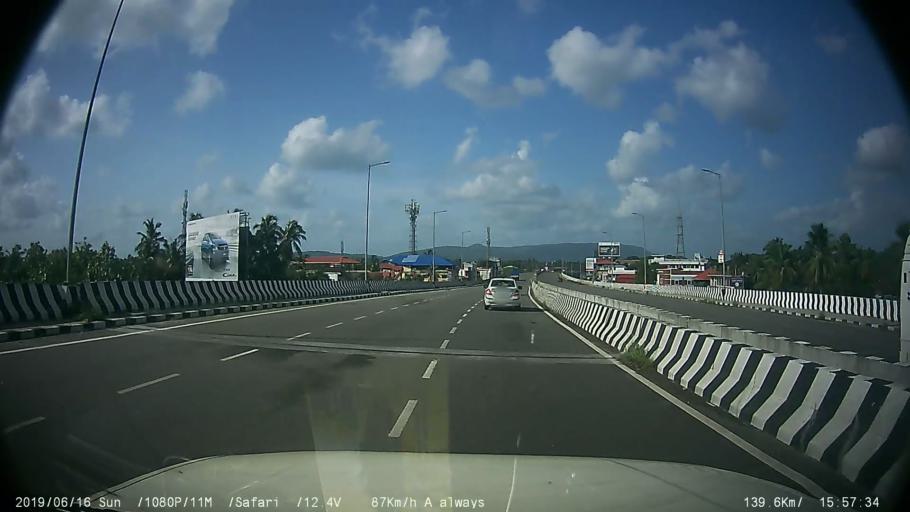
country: IN
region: Kerala
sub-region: Thrissur District
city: Trichur
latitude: 10.5314
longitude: 76.2591
